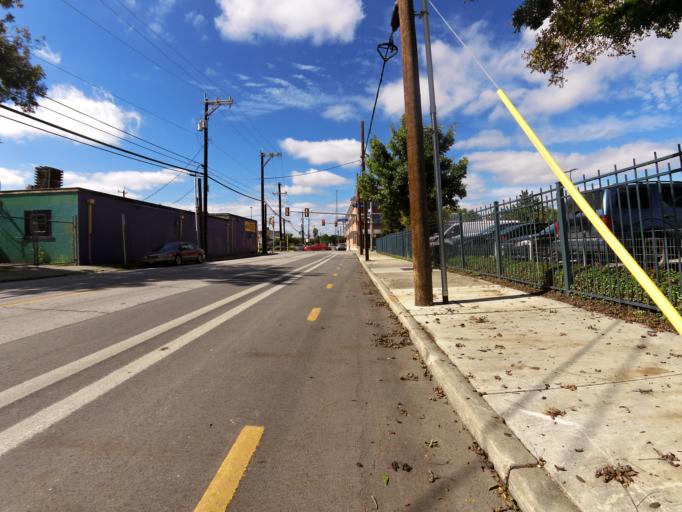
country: US
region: Texas
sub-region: Bexar County
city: San Antonio
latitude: 29.4170
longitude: -98.4973
